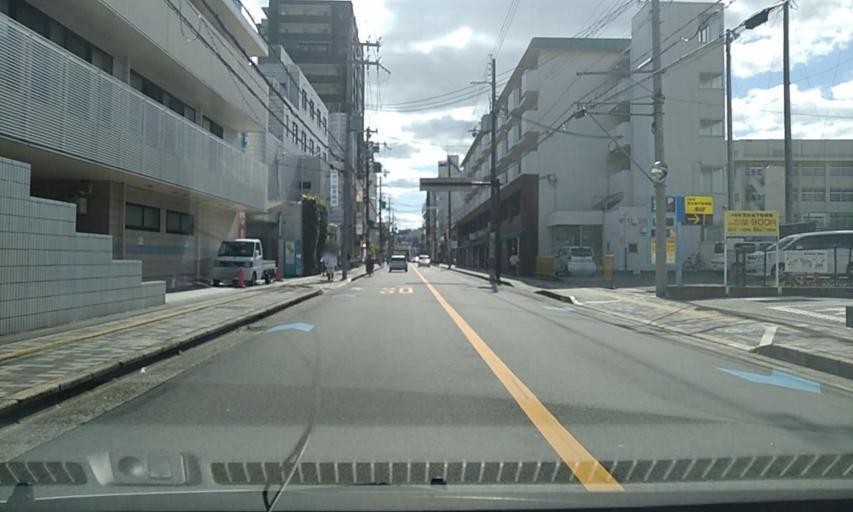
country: JP
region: Osaka
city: Ibaraki
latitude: 34.8187
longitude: 135.5614
